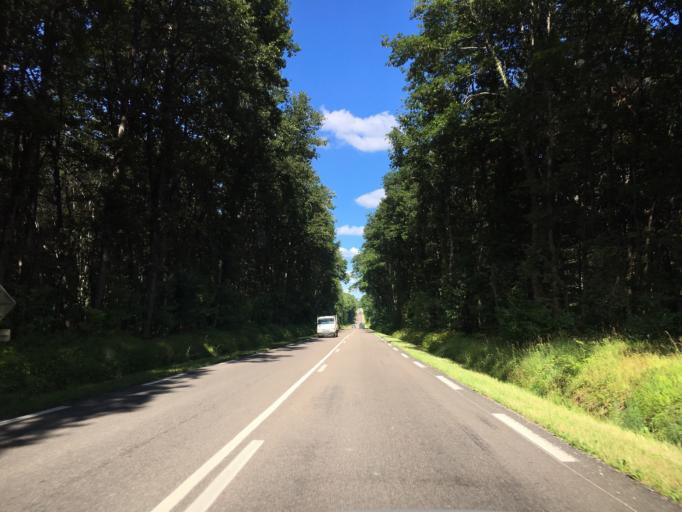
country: FR
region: Bourgogne
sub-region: Departement de l'Yonne
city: Pourrain
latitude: 47.7696
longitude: 3.4592
